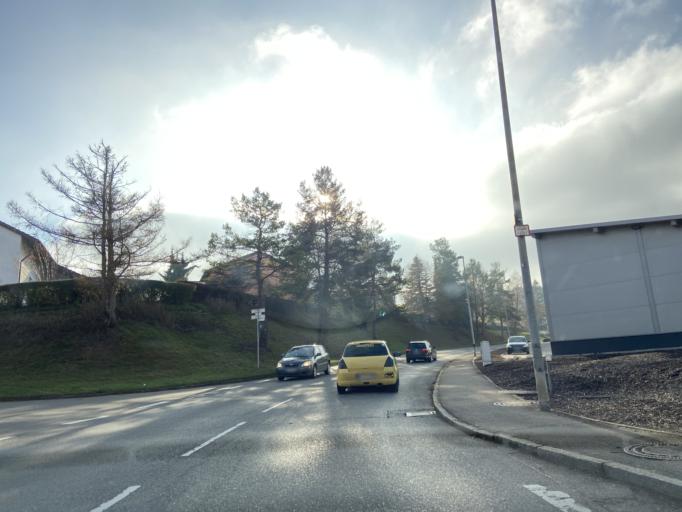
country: DE
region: Baden-Wuerttemberg
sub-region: Tuebingen Region
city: Gammertingen
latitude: 48.2445
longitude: 9.2218
